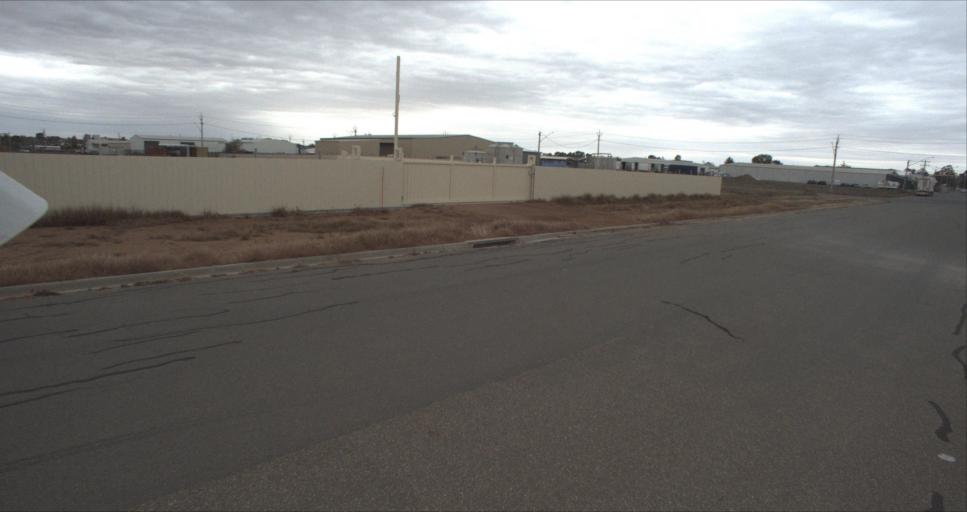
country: AU
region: New South Wales
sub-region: Leeton
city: Leeton
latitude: -34.5448
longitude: 146.3880
